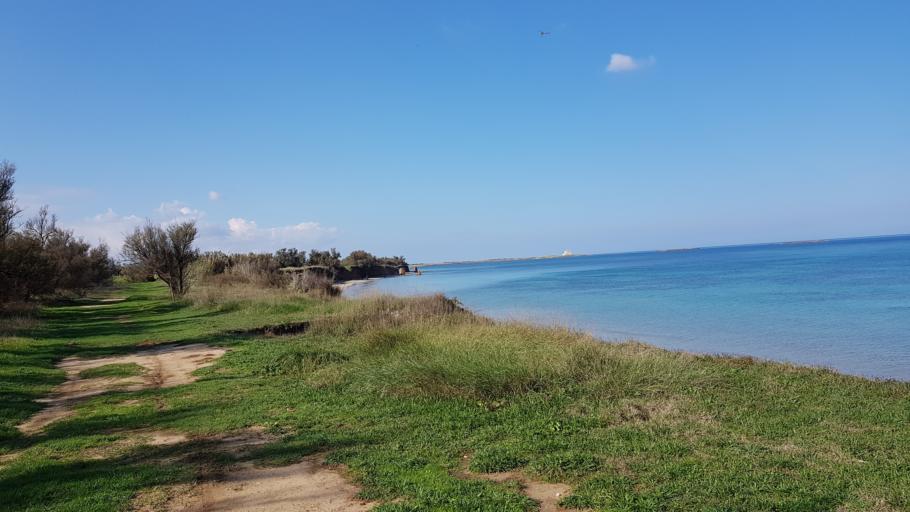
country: IT
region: Apulia
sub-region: Provincia di Brindisi
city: San Vito dei Normanni
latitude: 40.6999
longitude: 17.8168
